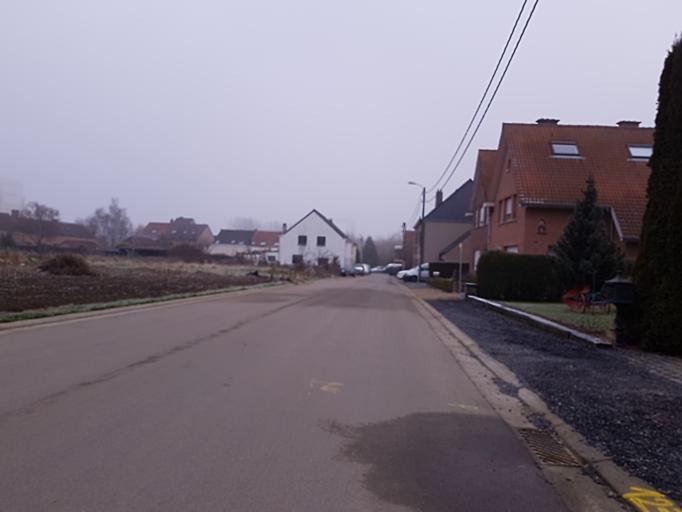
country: BE
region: Flanders
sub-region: Provincie Vlaams-Brabant
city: Vilvoorde
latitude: 50.9515
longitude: 4.4080
